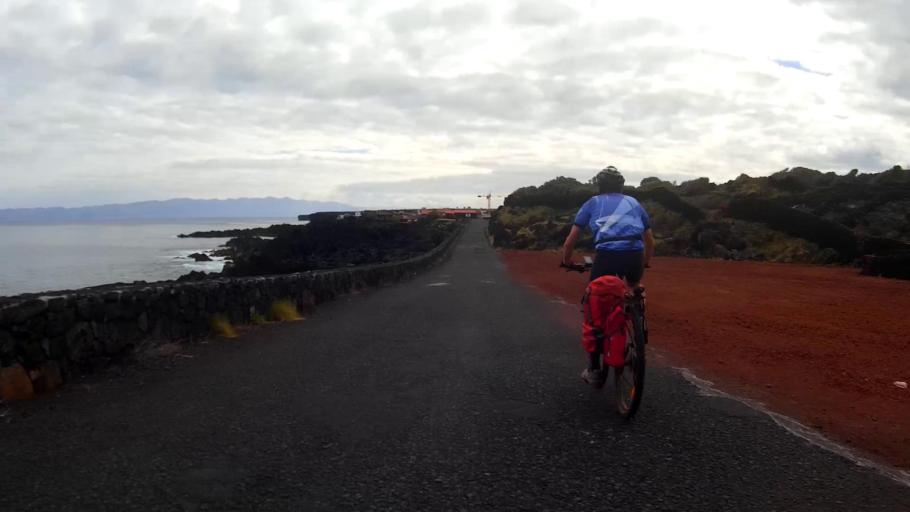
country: PT
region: Azores
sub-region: Madalena
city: Madalena
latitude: 38.5570
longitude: -28.4323
